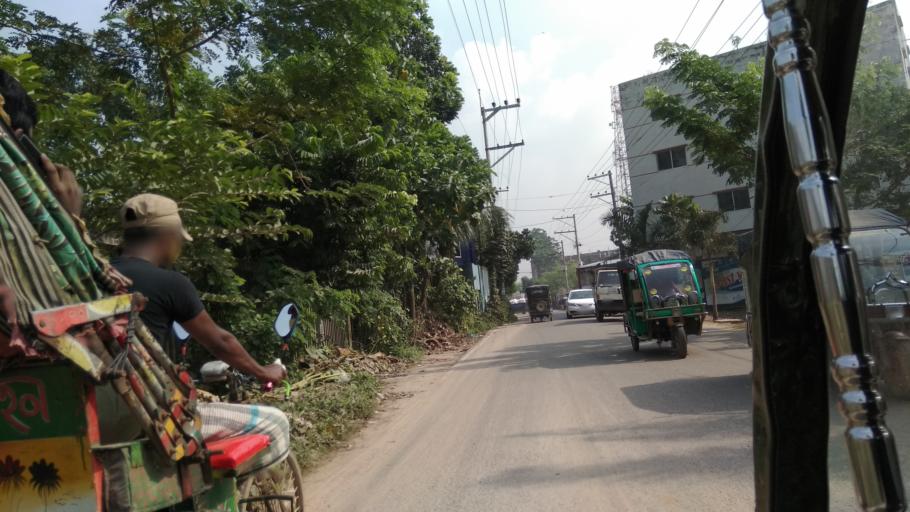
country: BD
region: Dhaka
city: Tungi
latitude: 23.9039
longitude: 90.2816
